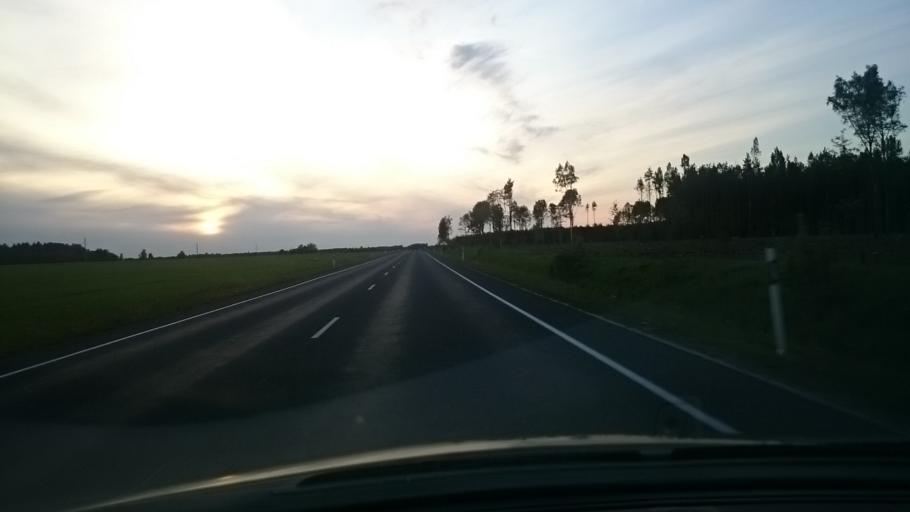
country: EE
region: Viljandimaa
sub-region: Vohma linn
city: Vohma
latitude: 58.7220
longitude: 25.6042
